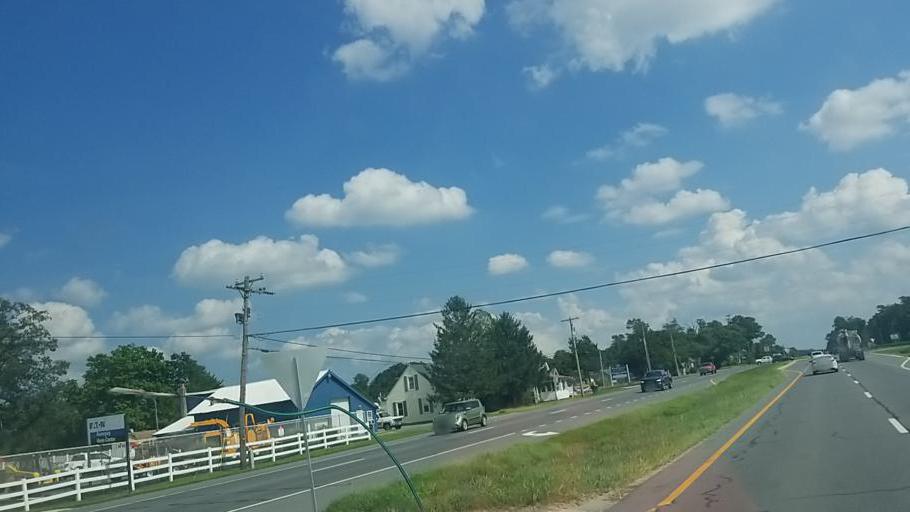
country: US
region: Delaware
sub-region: Sussex County
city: Georgetown
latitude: 38.6351
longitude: -75.3513
